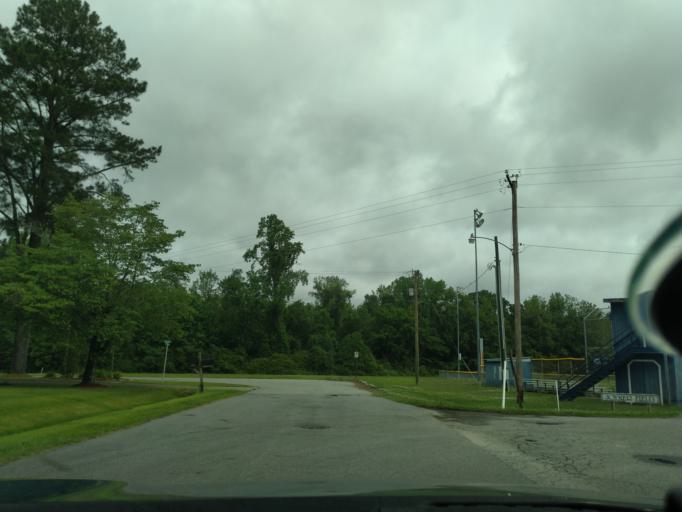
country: US
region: North Carolina
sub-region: Washington County
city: Plymouth
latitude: 35.8765
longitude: -76.7355
